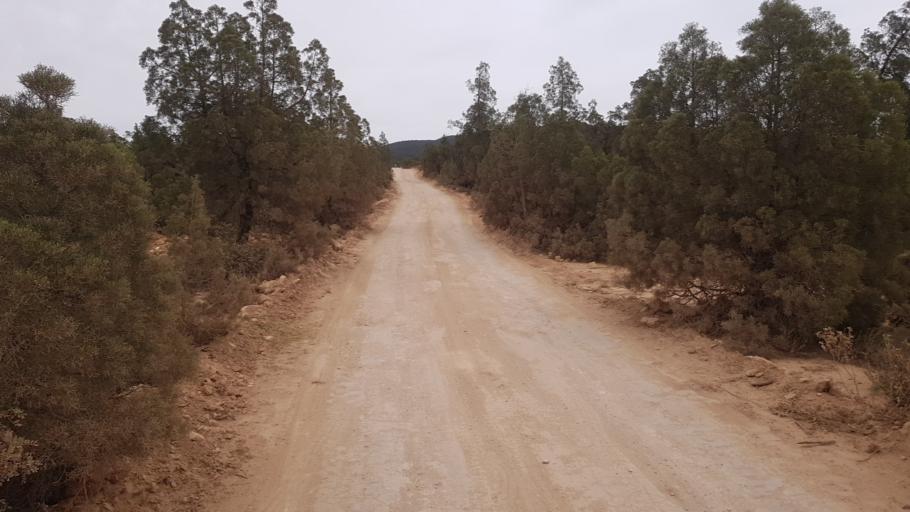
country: MA
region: Souss-Massa-Draa
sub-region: Agadir-Ida-ou-Tnan
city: Taghazout
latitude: 30.6415
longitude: -9.7103
